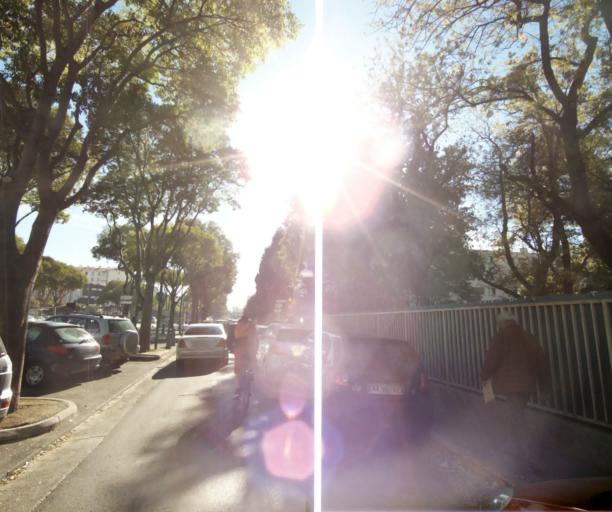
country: FR
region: Provence-Alpes-Cote d'Azur
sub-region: Departement des Bouches-du-Rhone
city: Marseille 08
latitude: 43.2685
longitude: 5.3933
